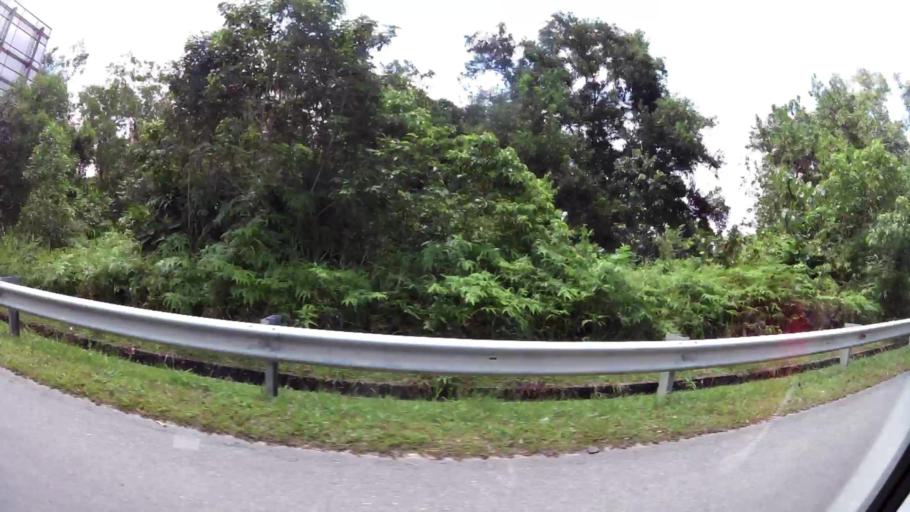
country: BN
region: Brunei and Muara
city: Bandar Seri Begawan
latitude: 4.9294
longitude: 114.9713
